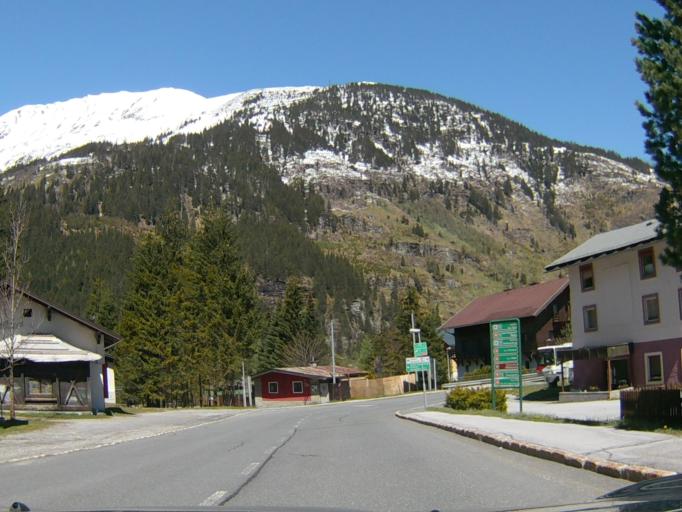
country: AT
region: Salzburg
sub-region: Politischer Bezirk Sankt Johann im Pongau
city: Bad Gastein
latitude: 47.0867
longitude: 13.1199
